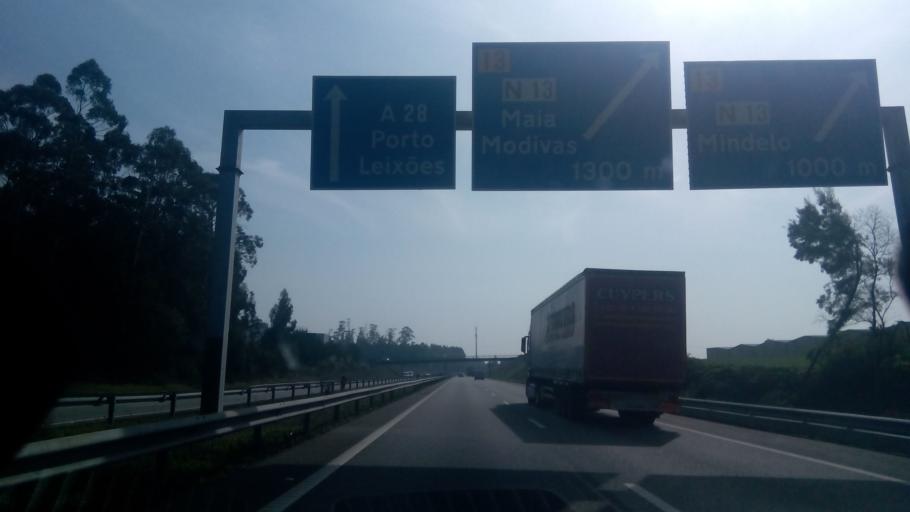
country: PT
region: Porto
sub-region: Vila do Conde
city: Arvore
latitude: 41.3135
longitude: -8.7014
